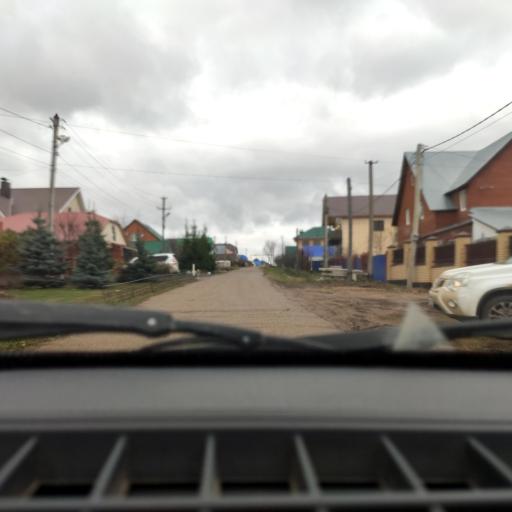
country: RU
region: Bashkortostan
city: Mikhaylovka
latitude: 54.8155
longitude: 55.8904
